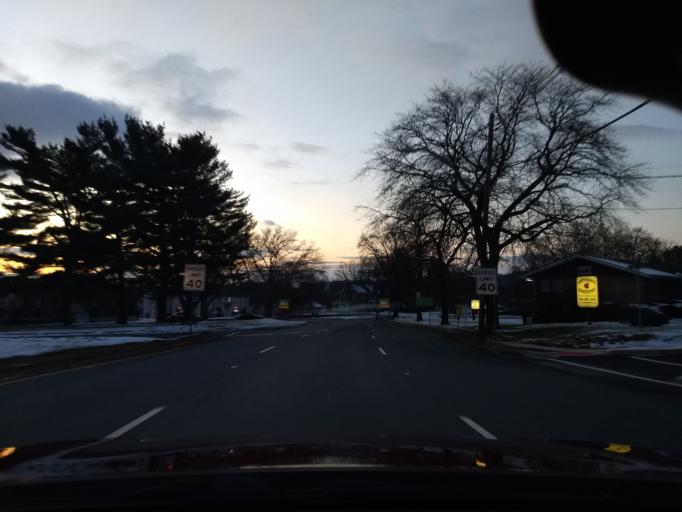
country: US
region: New Jersey
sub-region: Warren County
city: Phillipsburg
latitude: 40.6965
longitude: -75.1856
